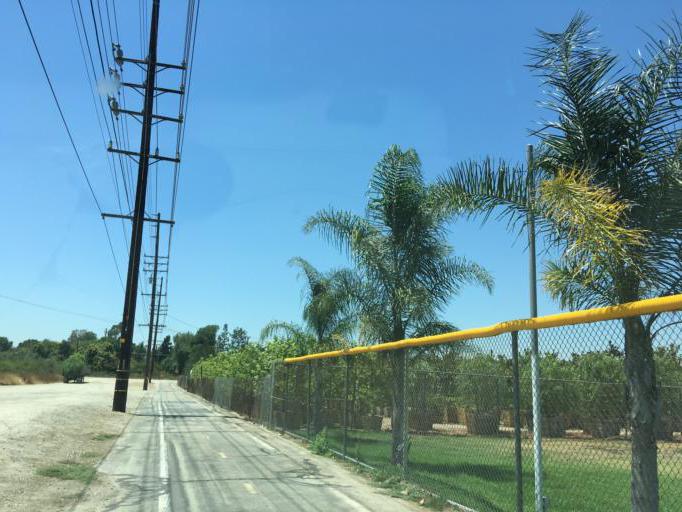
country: US
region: California
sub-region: Los Angeles County
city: South El Monte
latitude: 34.0519
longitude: -118.0694
